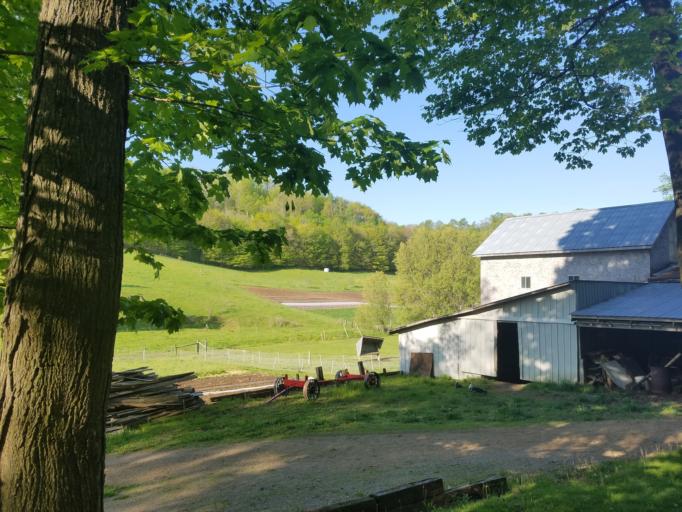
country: US
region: Wisconsin
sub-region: Monroe County
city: Tomah
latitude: 43.9490
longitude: -90.4928
